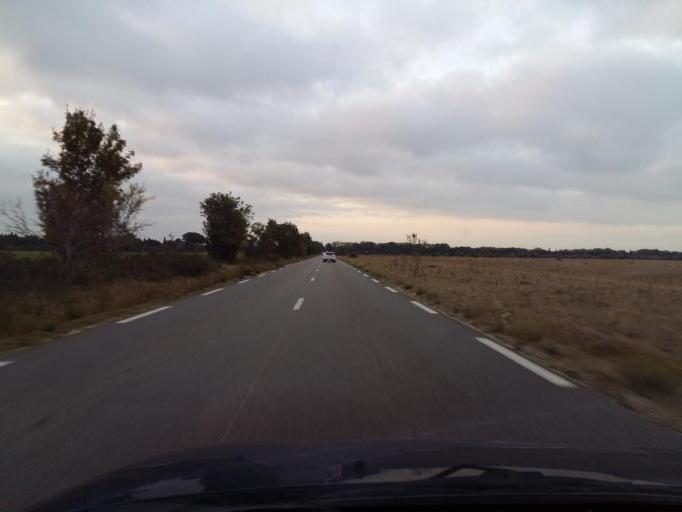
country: FR
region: Provence-Alpes-Cote d'Azur
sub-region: Departement des Bouches-du-Rhone
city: Miramas
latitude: 43.6269
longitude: 5.0174
